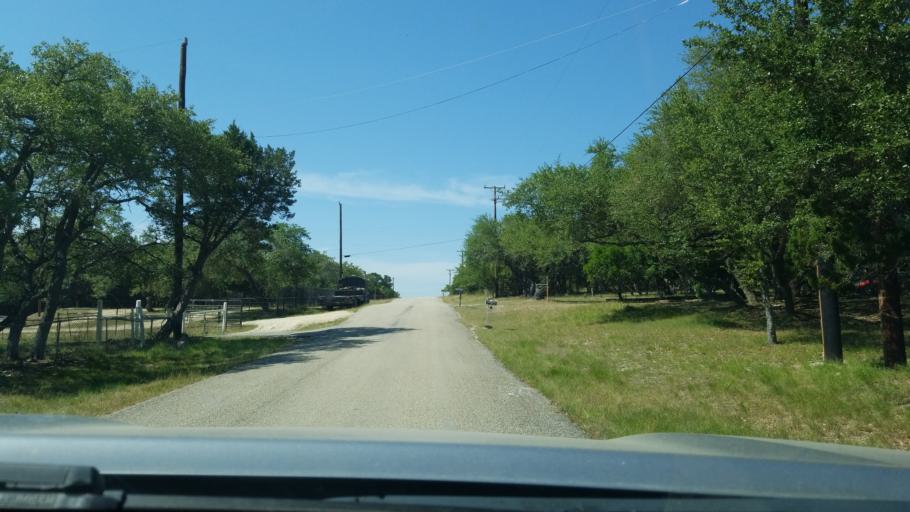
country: US
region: Texas
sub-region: Comal County
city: Bulverde
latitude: 29.7646
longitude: -98.5153
